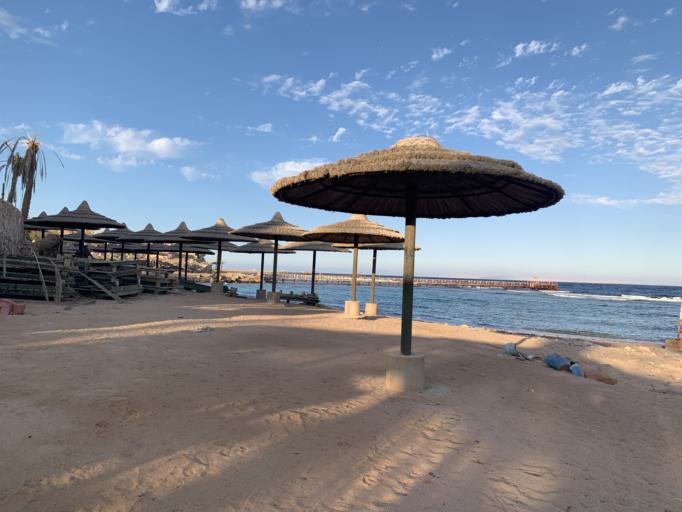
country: EG
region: South Sinai
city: Sharm el-Sheikh
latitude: 28.0151
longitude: 34.4391
